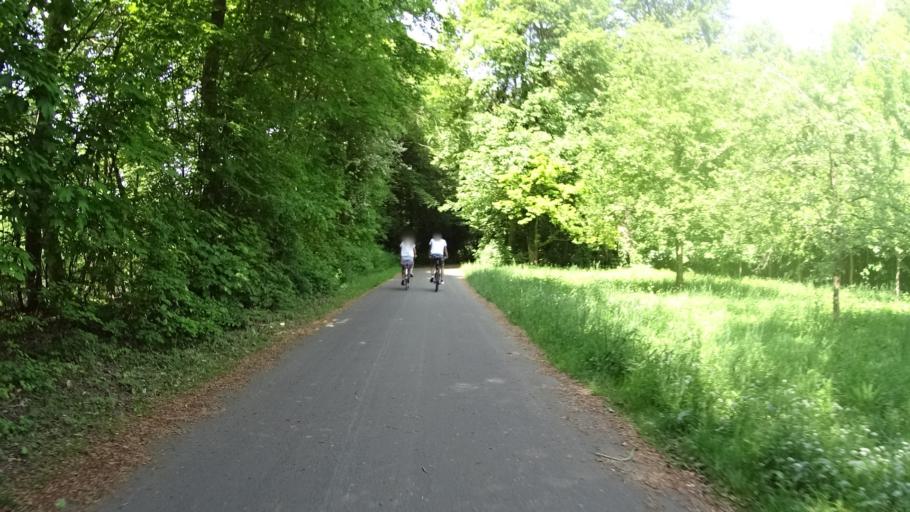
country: DE
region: Rheinland-Pfalz
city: Ludwigshafen am Rhein
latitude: 49.4535
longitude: 8.4523
